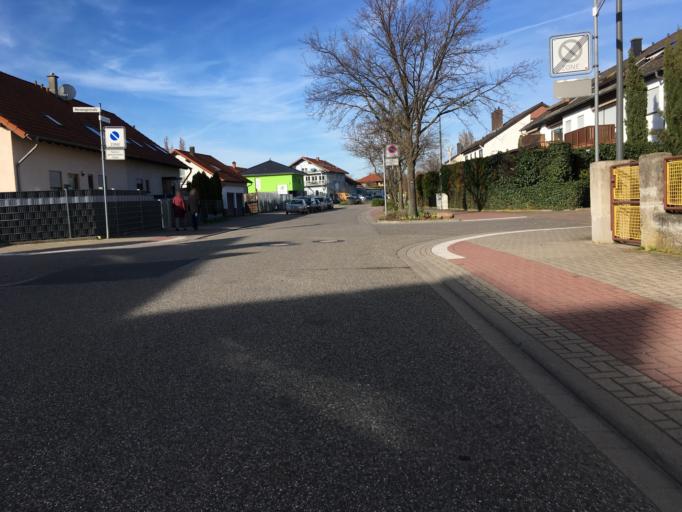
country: DE
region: Rheinland-Pfalz
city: Neustadt
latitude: 49.3523
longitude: 8.1649
